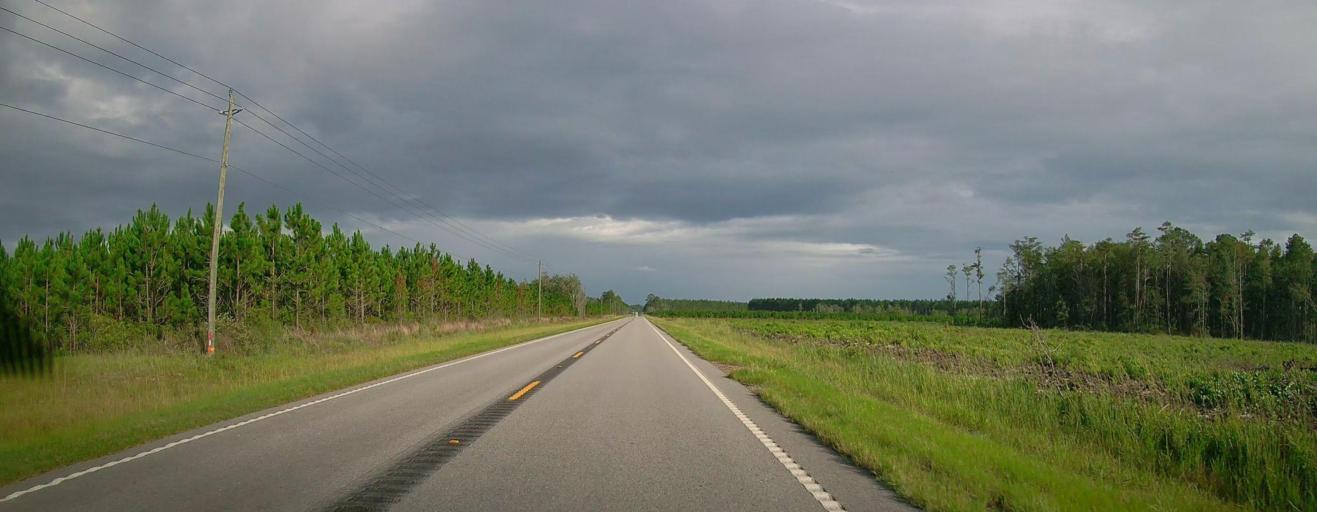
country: US
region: Georgia
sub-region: Coffee County
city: Nicholls
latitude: 31.3734
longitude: -82.6362
